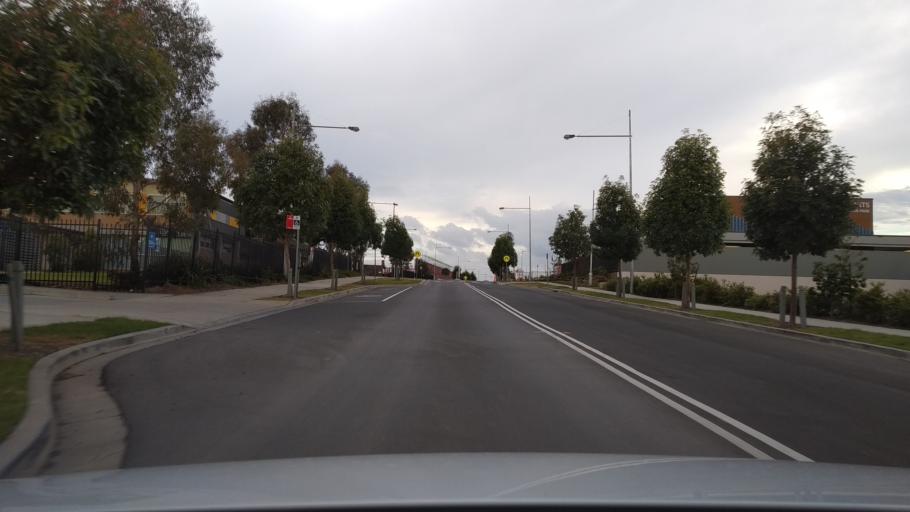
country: AU
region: New South Wales
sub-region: Camden
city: Narellan
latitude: -33.9965
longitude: 150.7347
